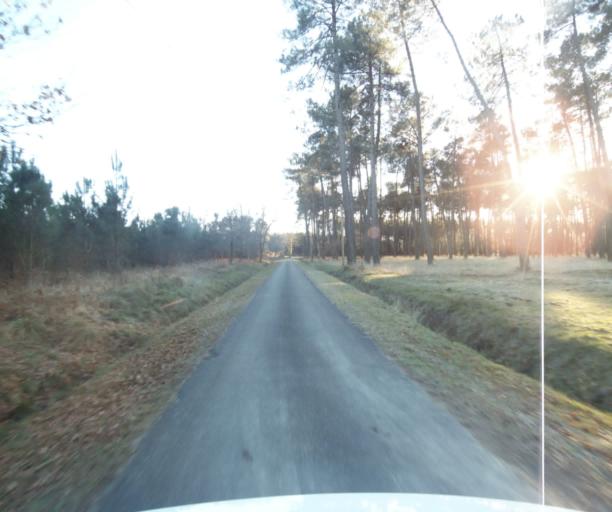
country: FR
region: Aquitaine
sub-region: Departement des Landes
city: Gabarret
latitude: 44.1034
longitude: -0.0802
